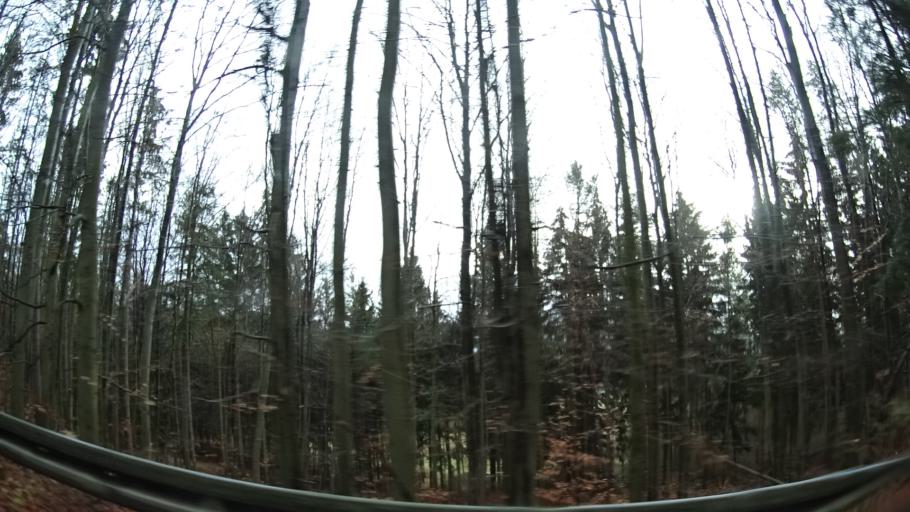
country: DE
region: Thuringia
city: Rippershausen
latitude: 50.6006
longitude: 10.3359
